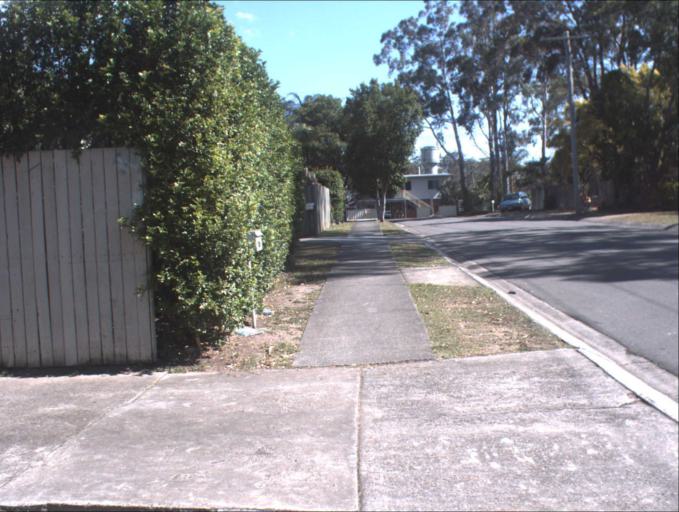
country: AU
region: Queensland
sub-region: Logan
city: Logan City
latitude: -27.6572
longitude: 153.1069
